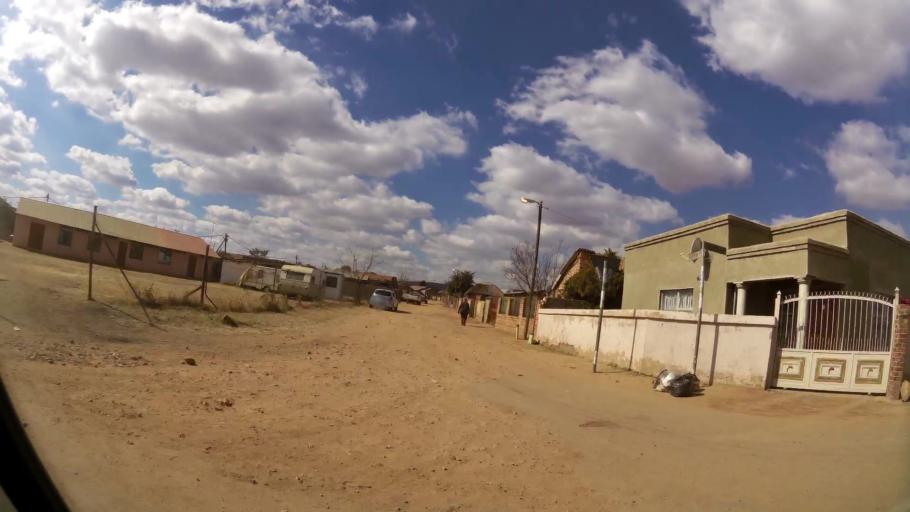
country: ZA
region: Gauteng
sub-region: City of Tshwane Metropolitan Municipality
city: Cullinan
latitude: -25.7070
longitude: 28.4031
